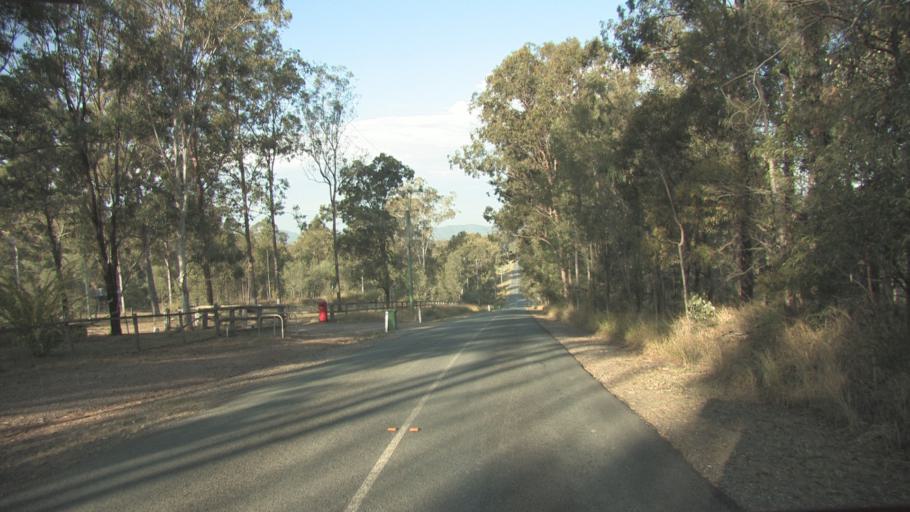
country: AU
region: Queensland
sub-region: Logan
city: Cedar Vale
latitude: -27.8457
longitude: 153.0893
